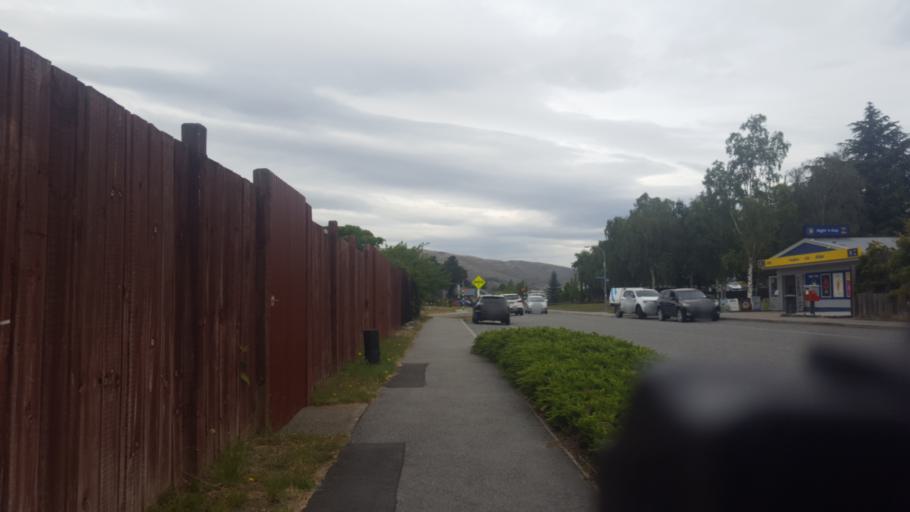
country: NZ
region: Otago
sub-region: Queenstown-Lakes District
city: Wanaka
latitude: -45.0417
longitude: 169.1892
